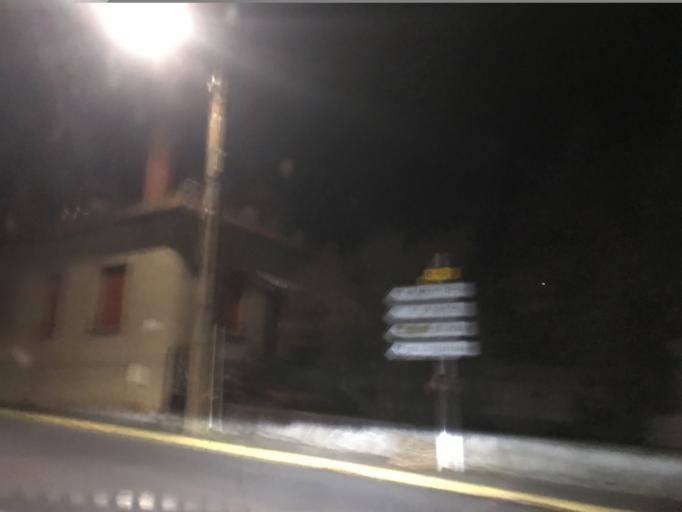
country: FR
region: Auvergne
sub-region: Departement du Puy-de-Dome
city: La Monnerie-le-Montel
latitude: 45.8705
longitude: 3.6073
